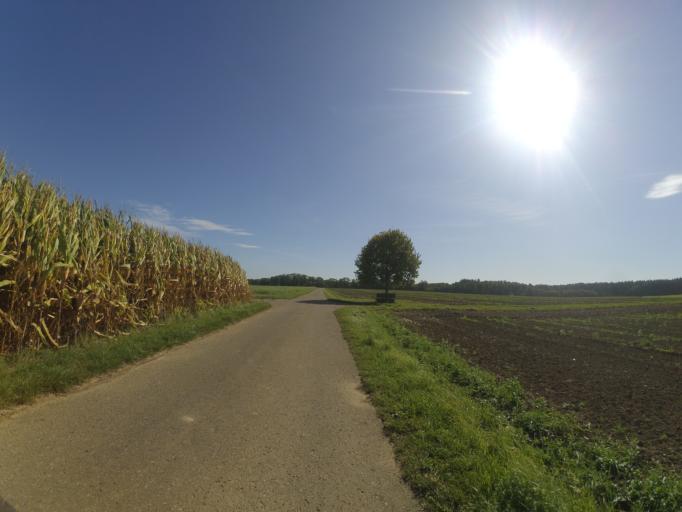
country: DE
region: Baden-Wuerttemberg
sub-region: Tuebingen Region
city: Neenstetten
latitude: 48.5444
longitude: 10.0311
